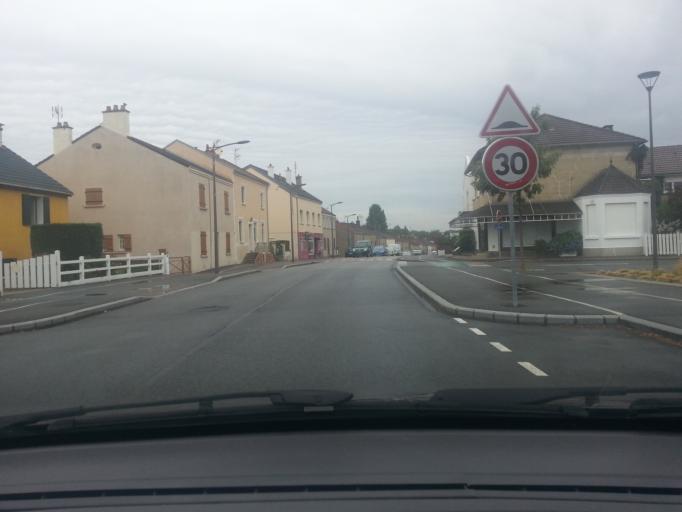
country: FR
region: Bourgogne
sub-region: Departement de Saone-et-Loire
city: Montchanin
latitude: 46.7518
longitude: 4.4725
